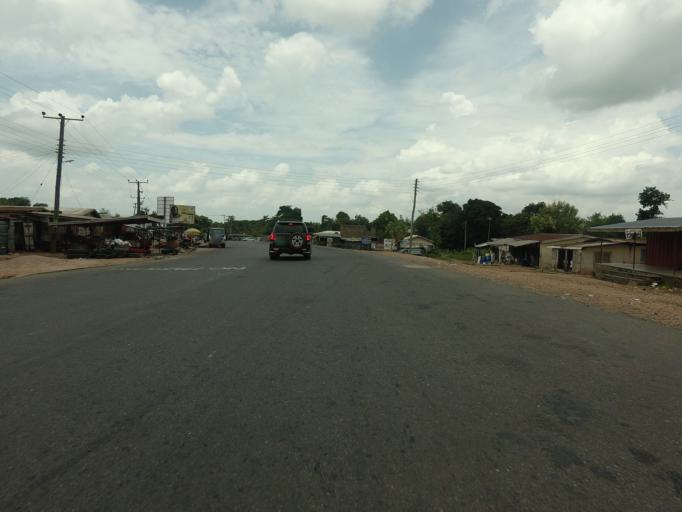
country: GH
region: Volta
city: Ho
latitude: 6.4166
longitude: 0.1723
